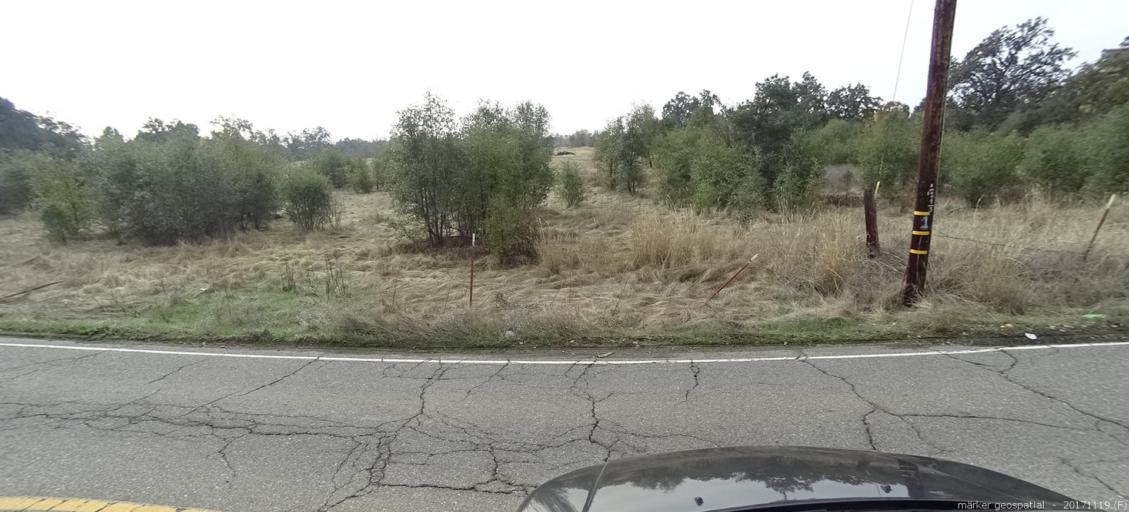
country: US
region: California
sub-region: Shasta County
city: Redding
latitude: 40.5347
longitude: -122.3350
